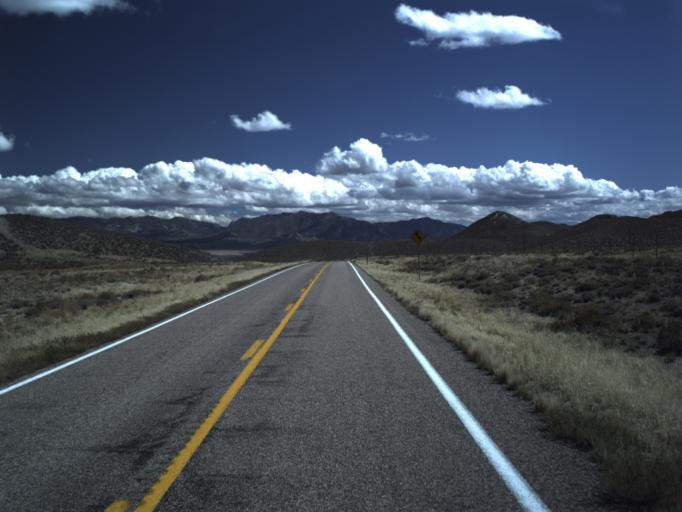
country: US
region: Utah
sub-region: Beaver County
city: Milford
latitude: 38.4261
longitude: -113.1180
